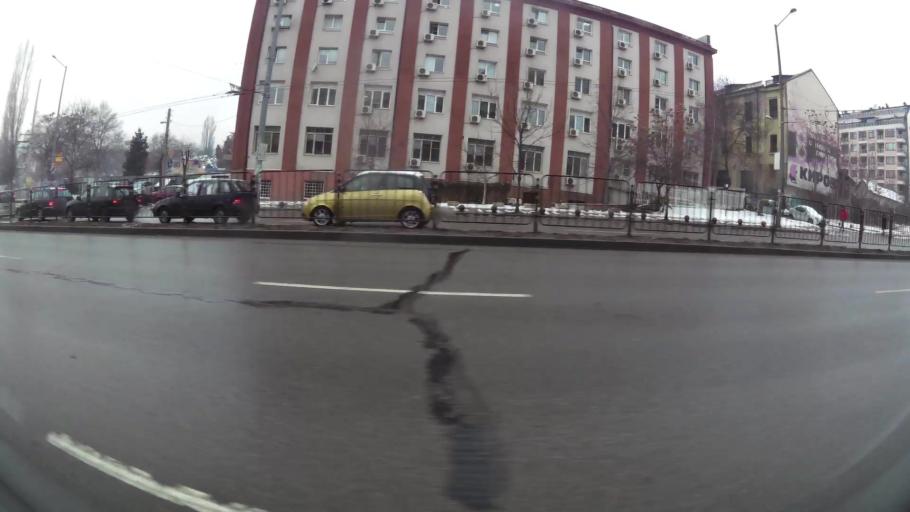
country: BG
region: Sofia-Capital
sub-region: Stolichna Obshtina
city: Sofia
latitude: 42.7069
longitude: 23.3126
